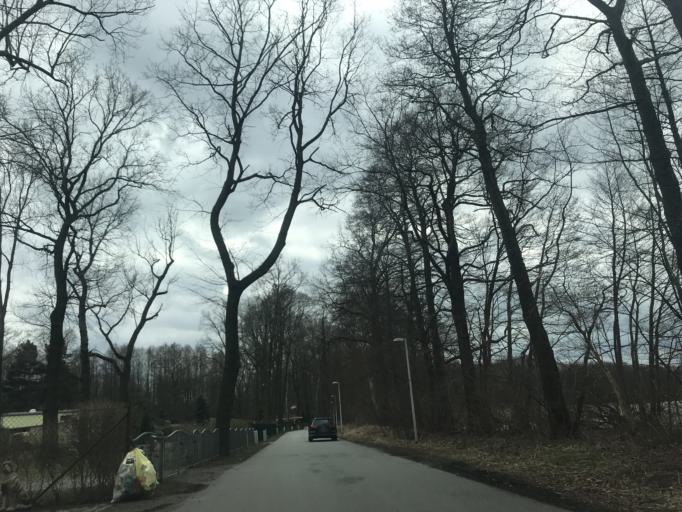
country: DE
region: Brandenburg
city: Zossen
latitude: 52.1463
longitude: 13.4757
